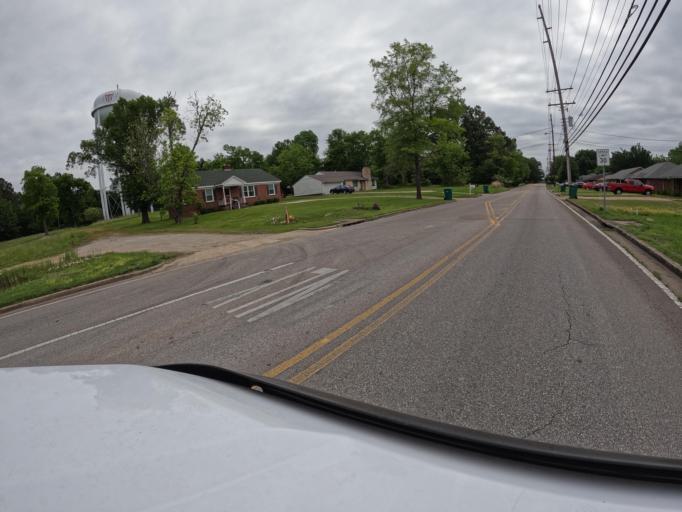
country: US
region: Mississippi
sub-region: Lee County
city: Tupelo
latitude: 34.2647
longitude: -88.7462
